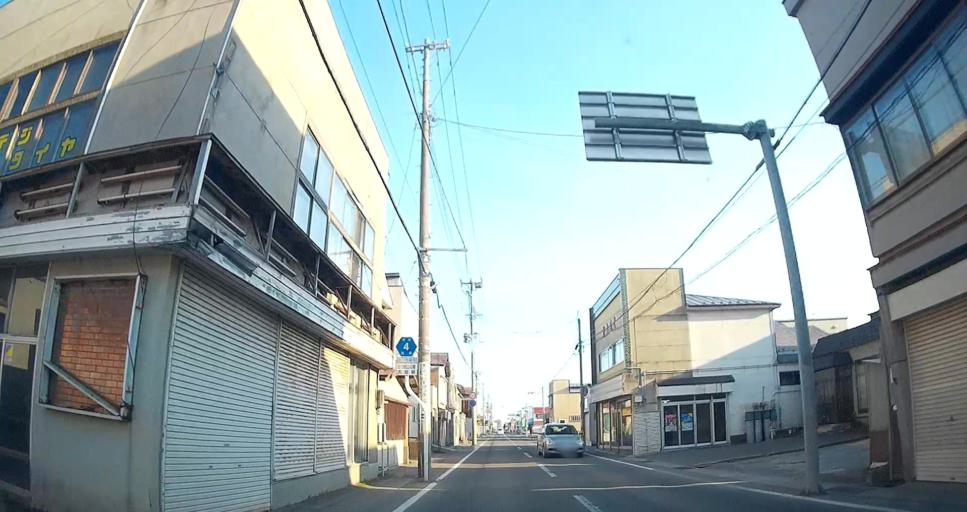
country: JP
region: Aomori
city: Mutsu
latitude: 41.2922
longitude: 141.2107
